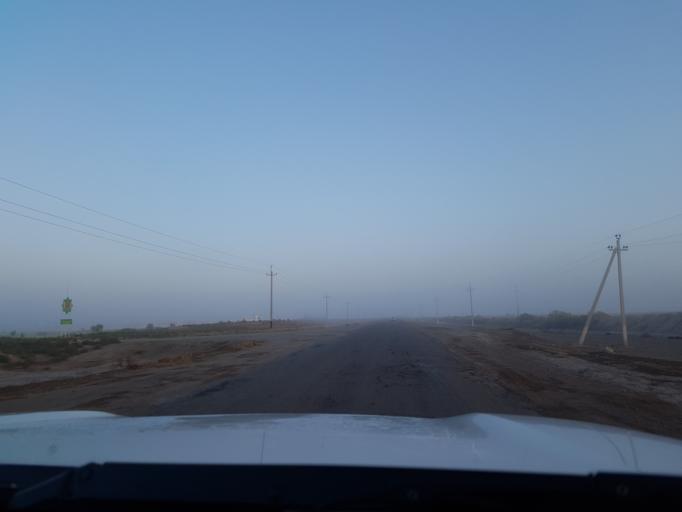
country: TM
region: Dasoguz
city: Koeneuergench
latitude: 41.8146
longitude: 58.7032
